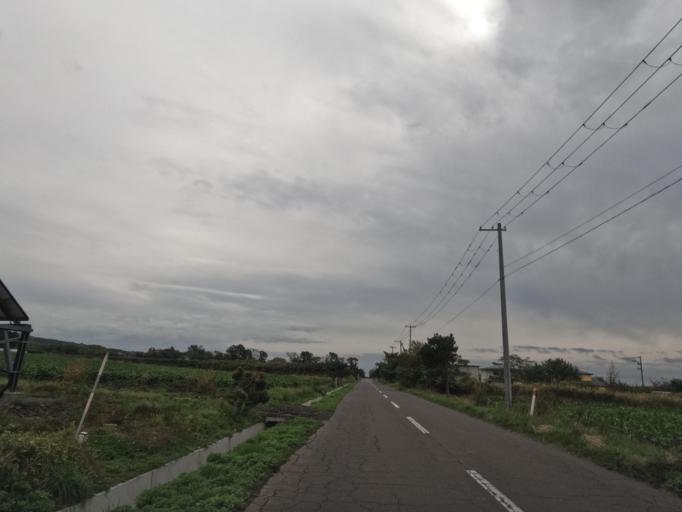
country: JP
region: Hokkaido
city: Date
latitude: 42.4364
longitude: 140.9074
